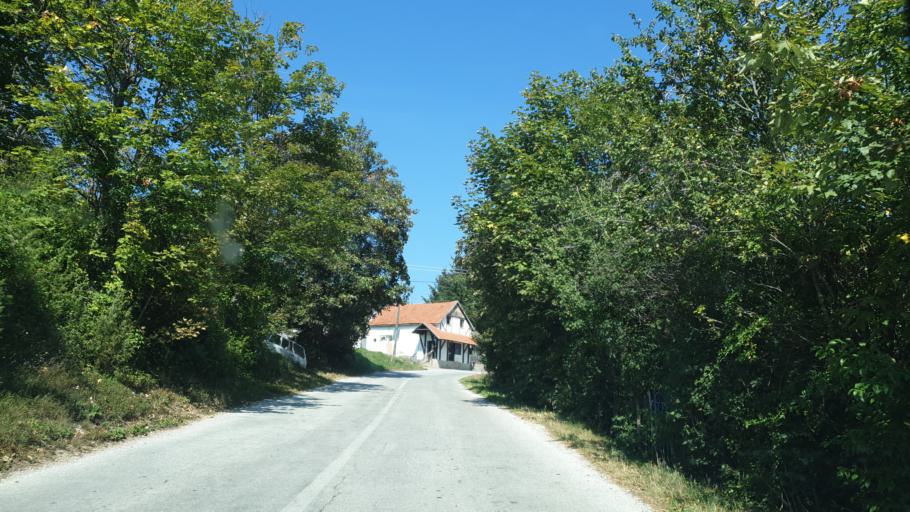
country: RS
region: Central Serbia
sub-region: Zlatiborski Okrug
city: Cajetina
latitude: 43.7198
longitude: 19.8338
